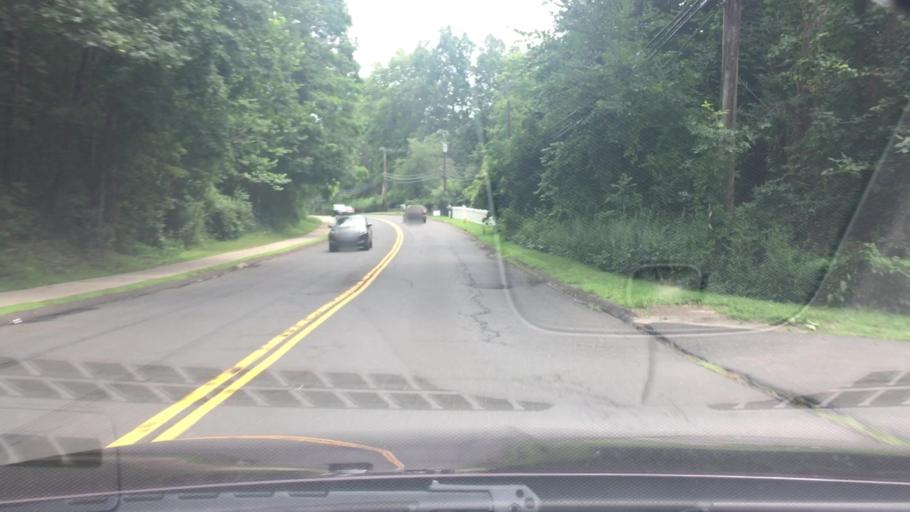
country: US
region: Connecticut
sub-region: Fairfield County
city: Danbury
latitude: 41.4290
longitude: -73.4235
